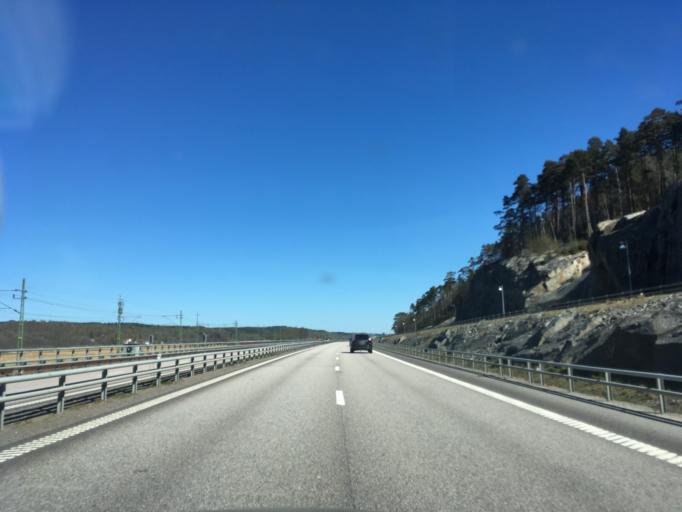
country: SE
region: Vaestra Goetaland
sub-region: Ale Kommun
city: Nodinge-Nol
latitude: 57.8835
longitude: 12.0395
